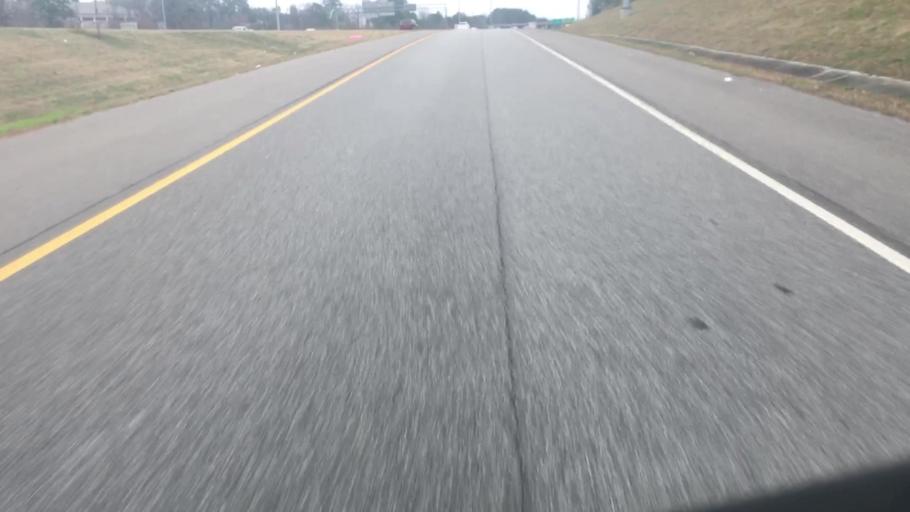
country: US
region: Alabama
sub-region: Jefferson County
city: Hoover
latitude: 33.3854
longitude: -86.8037
